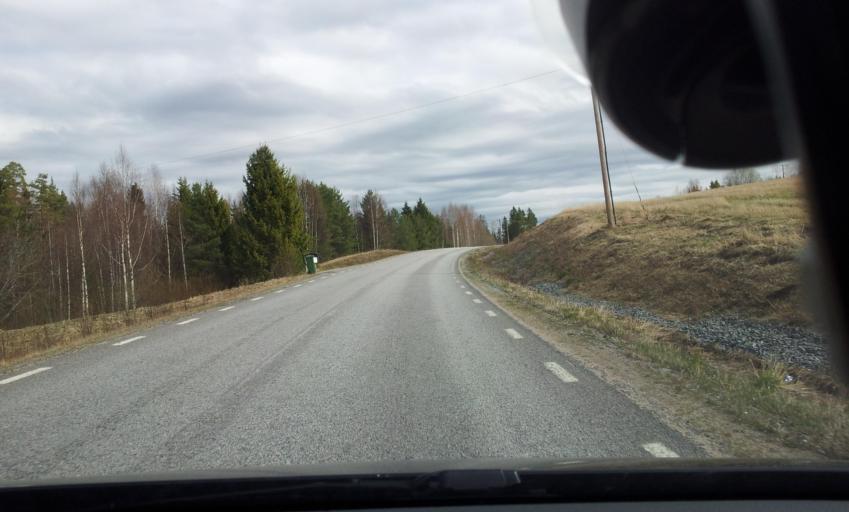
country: SE
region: Gaevleborg
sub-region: Ljusdals Kommun
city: Ljusdal
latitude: 61.7689
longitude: 16.0169
